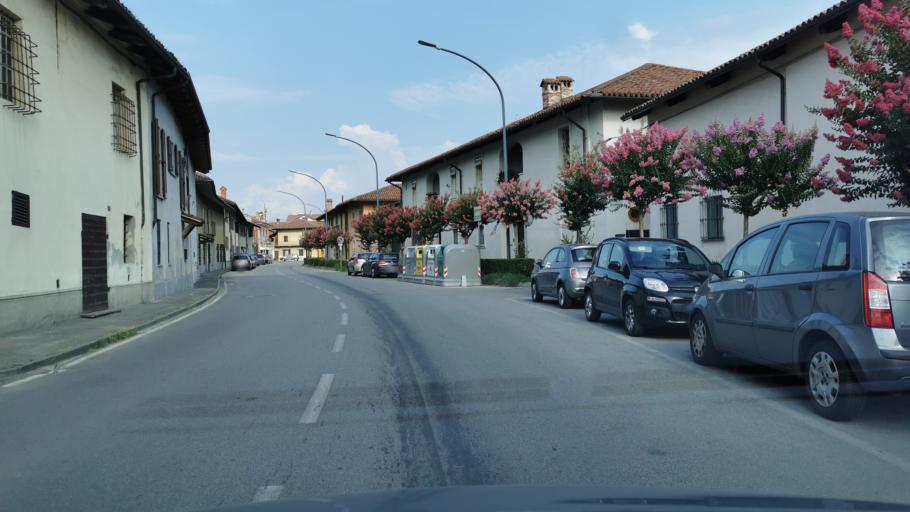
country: IT
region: Piedmont
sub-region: Provincia di Torino
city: Vigone
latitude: 44.8424
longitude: 7.4988
